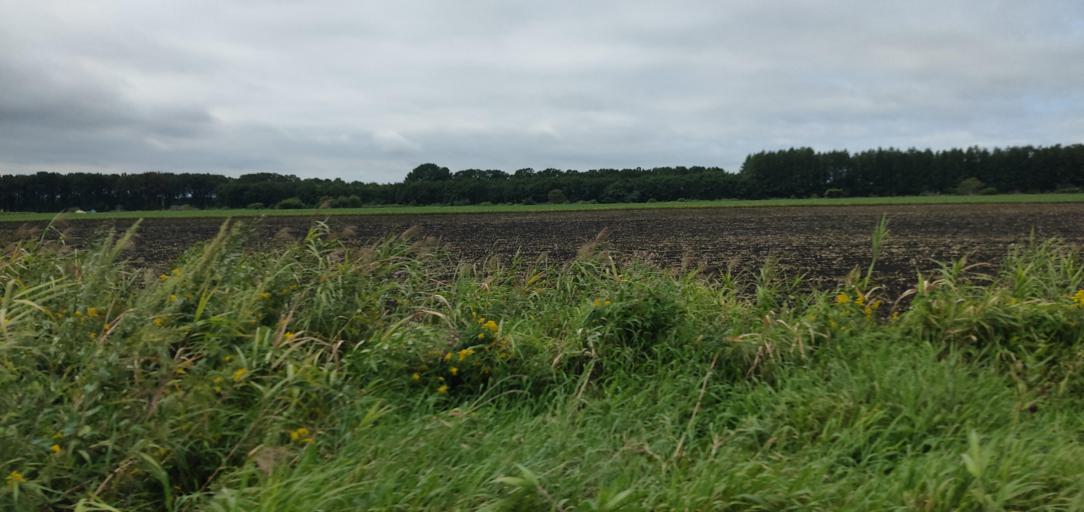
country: JP
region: Hokkaido
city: Otofuke
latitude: 43.0772
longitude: 143.2254
